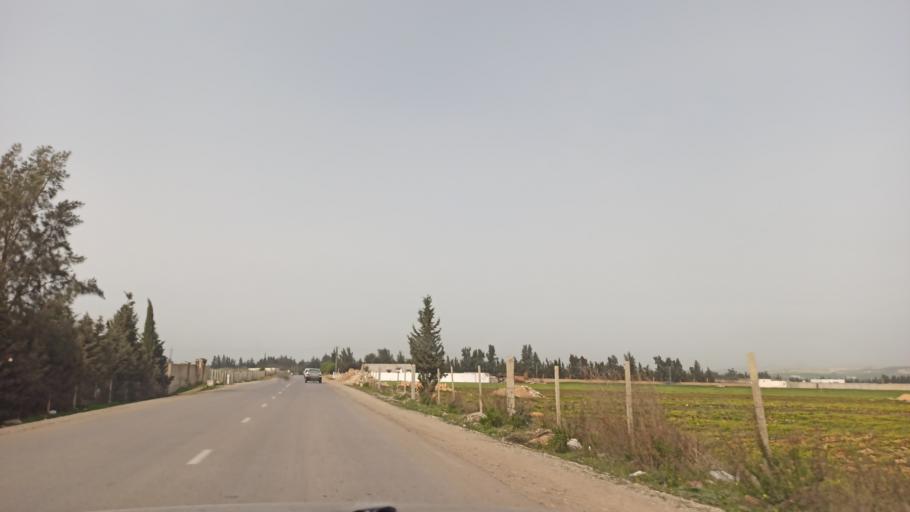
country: TN
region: Zaghwan
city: Zaghouan
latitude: 36.4198
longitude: 10.1018
